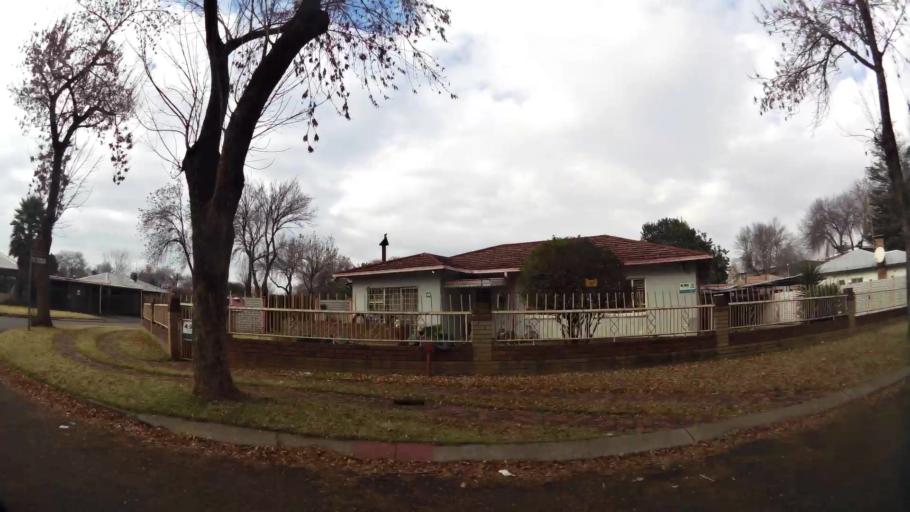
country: ZA
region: Gauteng
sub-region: Sedibeng District Municipality
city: Vanderbijlpark
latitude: -26.7011
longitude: 27.8277
